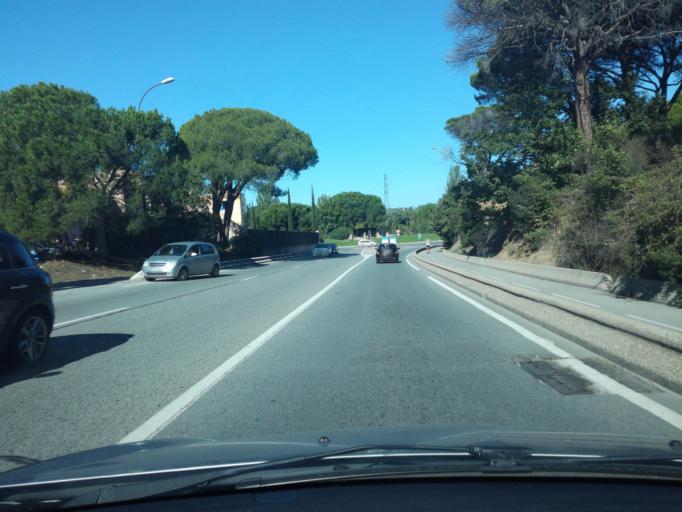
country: FR
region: Provence-Alpes-Cote d'Azur
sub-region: Departement du Var
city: Frejus
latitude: 43.4426
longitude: 6.7405
